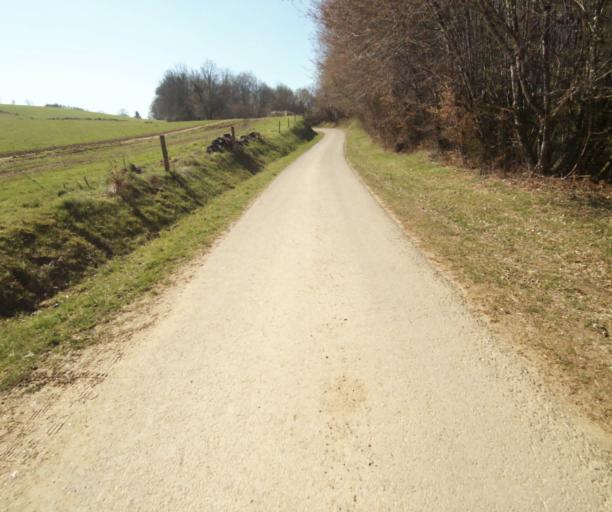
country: FR
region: Limousin
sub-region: Departement de la Correze
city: Saint-Mexant
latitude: 45.3197
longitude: 1.6062
